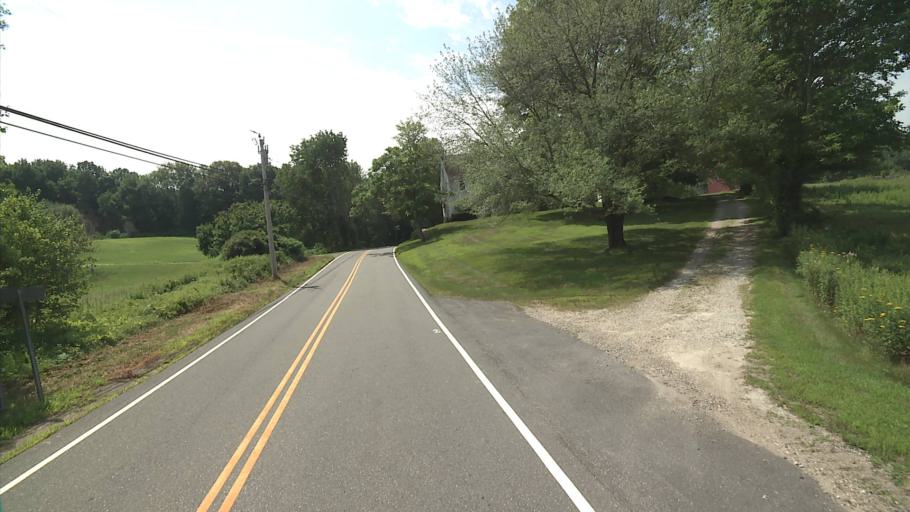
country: US
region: Connecticut
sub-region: Windham County
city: Danielson
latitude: 41.7901
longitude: -71.8332
